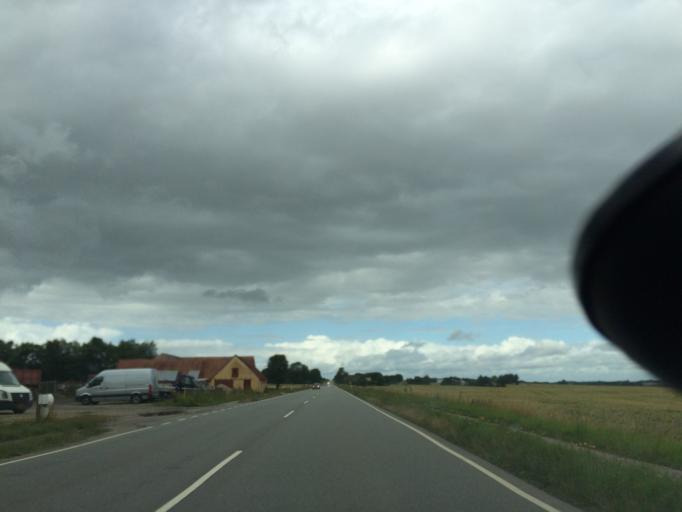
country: DK
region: Central Jutland
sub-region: Skanderborg Kommune
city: Galten
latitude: 56.1485
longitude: 9.8628
